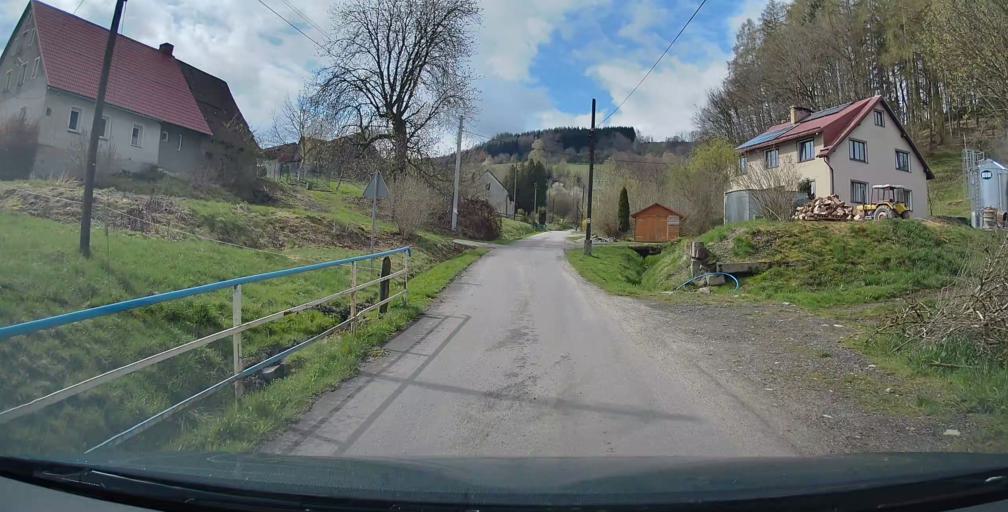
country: PL
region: Lower Silesian Voivodeship
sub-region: Powiat klodzki
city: Lewin Klodzki
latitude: 50.4024
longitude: 16.2653
